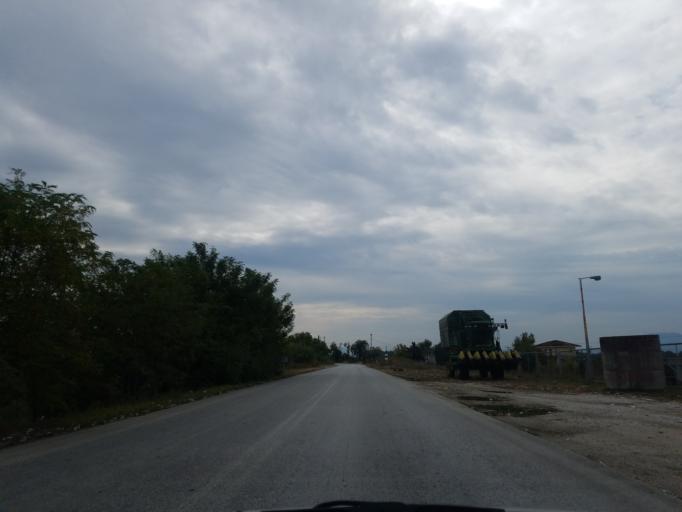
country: GR
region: Thessaly
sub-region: Nomos Kardhitsas
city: Sofades
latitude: 39.3313
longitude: 22.0873
